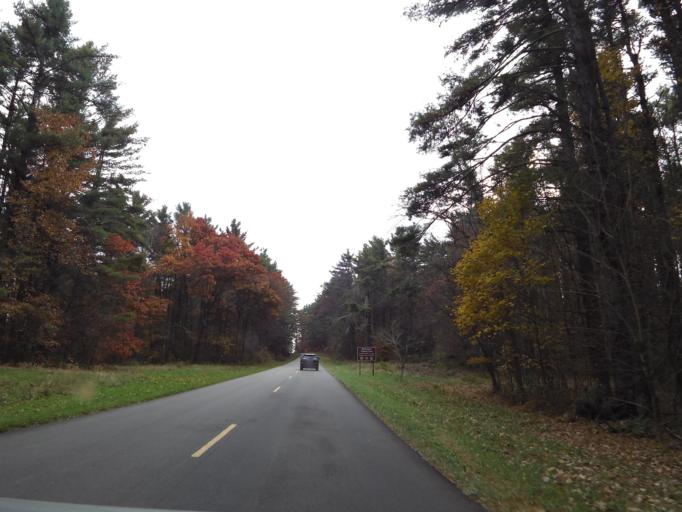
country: US
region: North Carolina
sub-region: Ashe County
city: Jefferson
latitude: 36.3481
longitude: -81.3740
